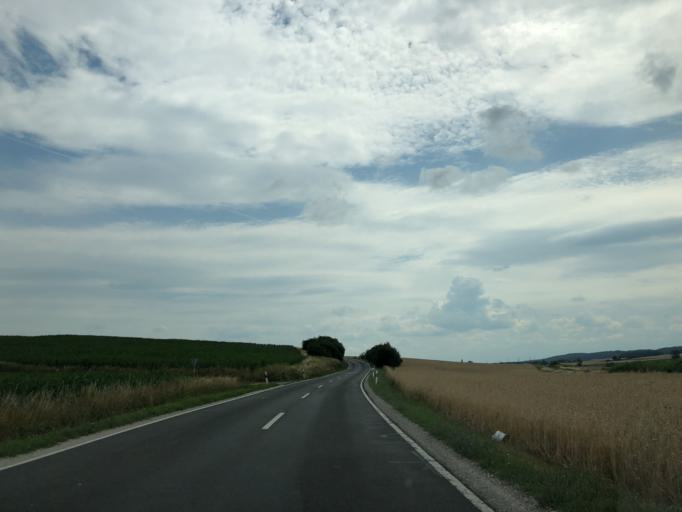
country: DE
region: Bavaria
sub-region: Regierungsbezirk Mittelfranken
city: Wachenroth
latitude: 49.7489
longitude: 10.6905
